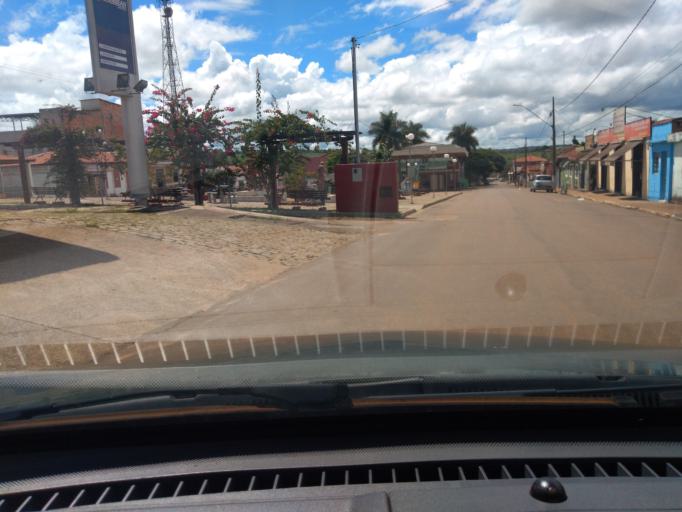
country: BR
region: Minas Gerais
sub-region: Tres Coracoes
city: Tres Coracoes
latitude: -21.5843
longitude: -45.0730
